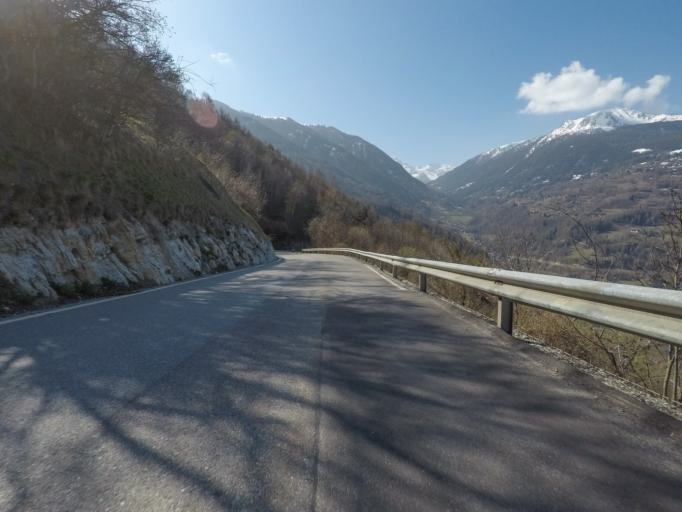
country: CH
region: Valais
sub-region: Conthey District
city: Basse-Nendaz
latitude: 46.1940
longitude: 7.3316
